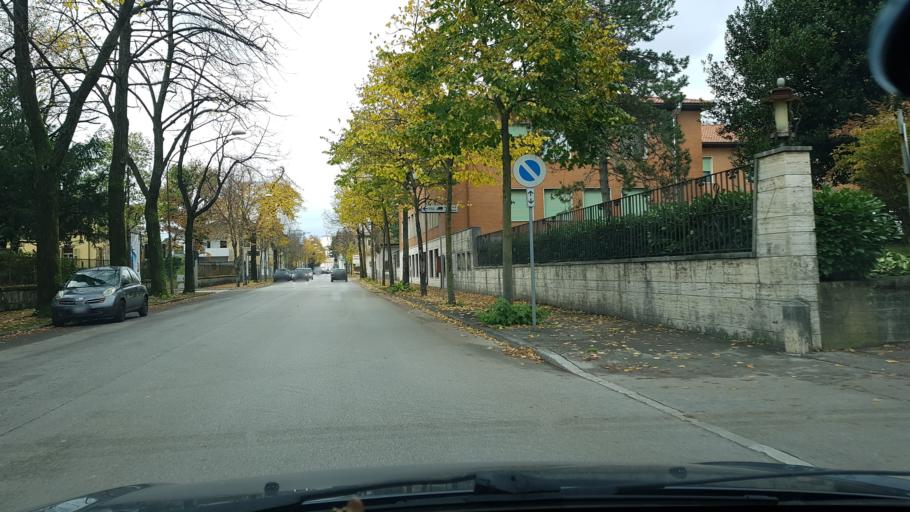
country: SI
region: Sempeter-Vrtojba
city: Sempeter pri Gorici
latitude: 45.9343
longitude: 13.6330
